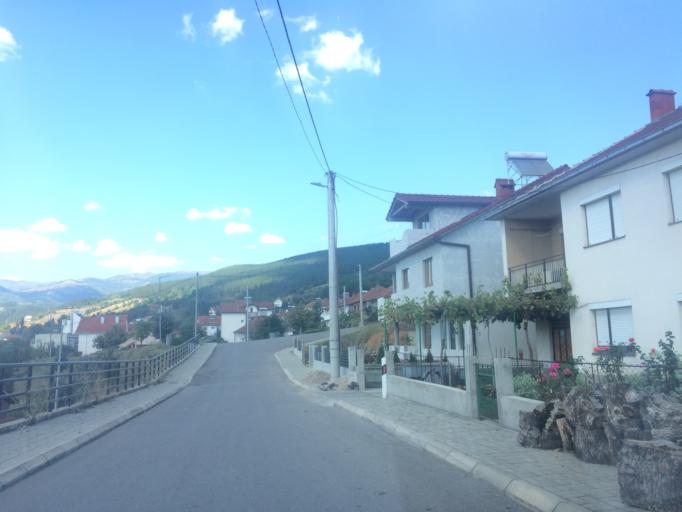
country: MK
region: Makedonska Kamenica
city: Makedonska Kamenica
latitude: 42.0183
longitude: 22.5918
